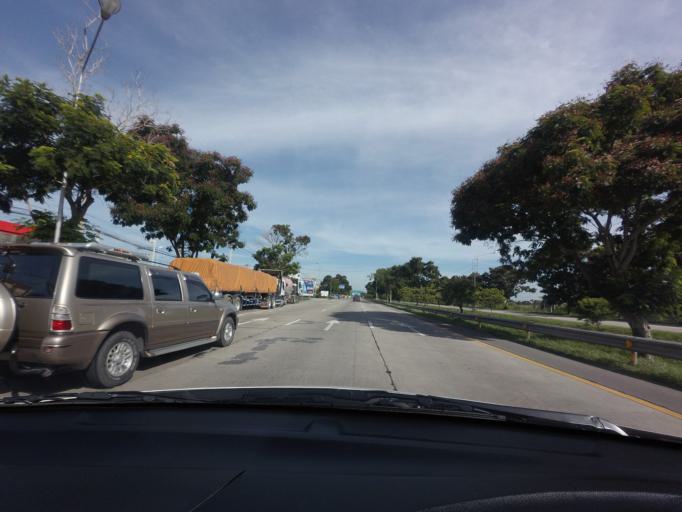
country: TH
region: Suphan Buri
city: Bang Pla Ma
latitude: 14.4033
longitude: 100.1611
